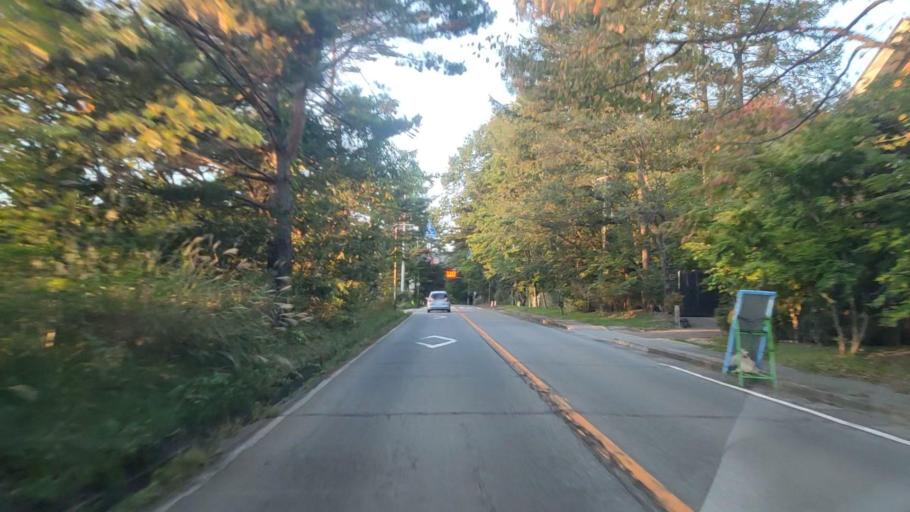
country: JP
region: Nagano
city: Komoro
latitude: 36.3688
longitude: 138.5875
